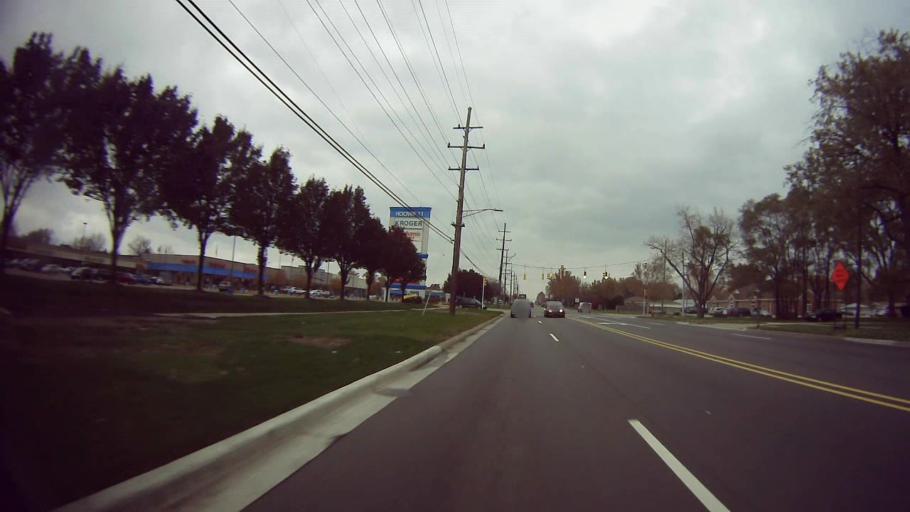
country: US
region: Michigan
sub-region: Macomb County
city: Center Line
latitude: 42.4871
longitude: -83.0064
